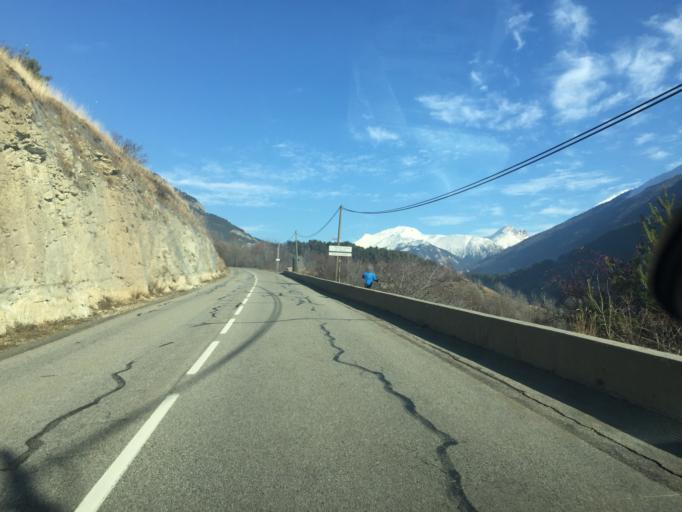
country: FR
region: Rhone-Alpes
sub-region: Departement de la Savoie
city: Modane
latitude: 45.2075
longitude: 6.6778
